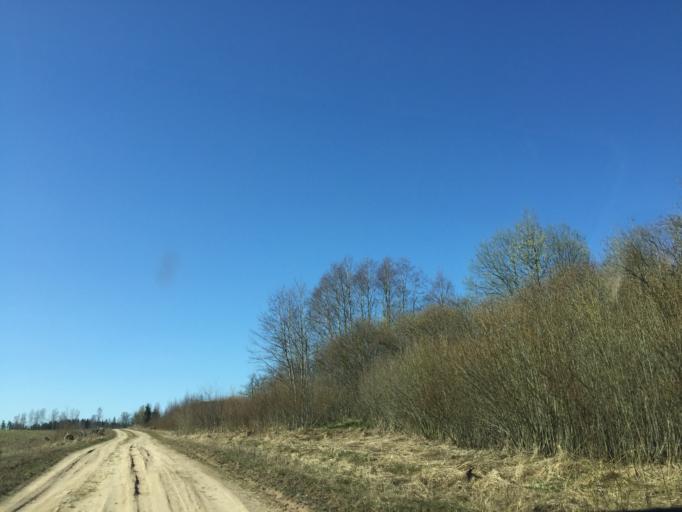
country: LV
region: Malpils
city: Malpils
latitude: 57.0394
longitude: 25.0741
